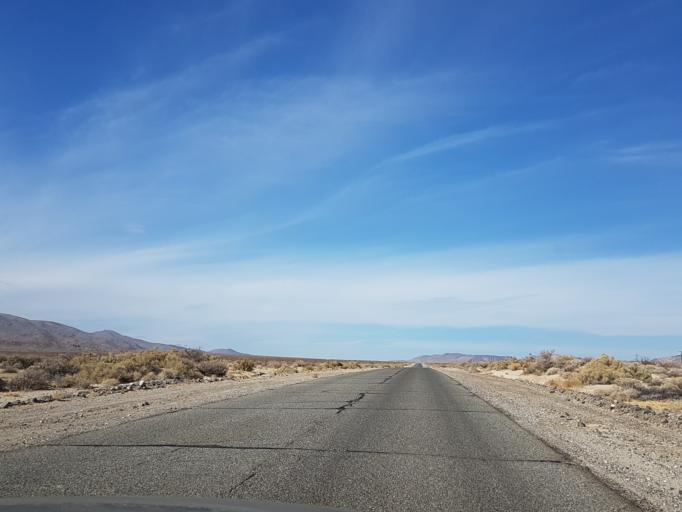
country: US
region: California
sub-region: San Bernardino County
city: Searles Valley
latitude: 35.8536
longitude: -117.3356
